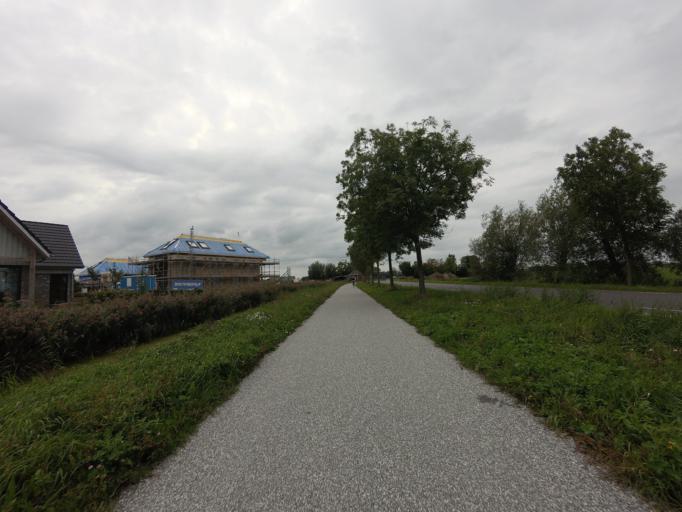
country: NL
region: Friesland
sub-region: Sudwest Fryslan
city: IJlst
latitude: 53.0412
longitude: 5.6269
